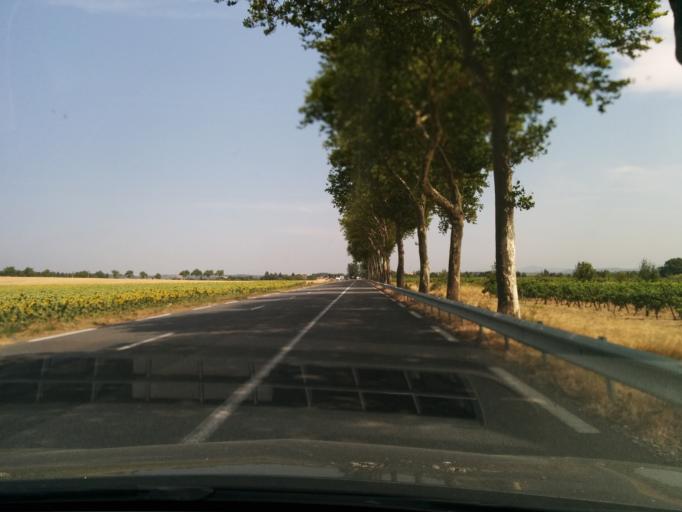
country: FR
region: Languedoc-Roussillon
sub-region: Departement de l'Aude
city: Pezens
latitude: 43.2597
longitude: 2.2397
